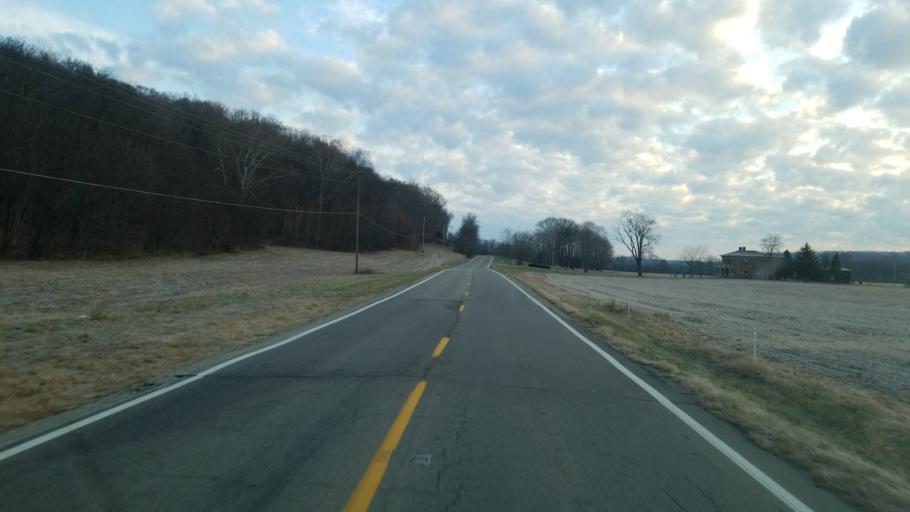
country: US
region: Ohio
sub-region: Ross County
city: Frankfort
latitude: 39.2448
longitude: -83.2135
